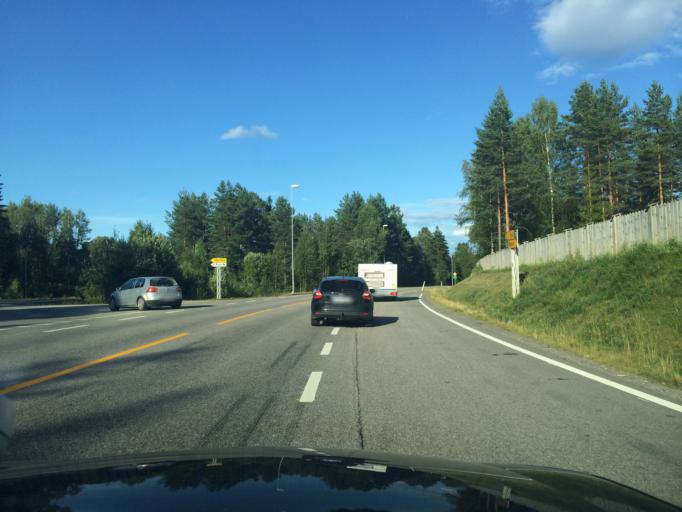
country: NO
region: Hedmark
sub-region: Elverum
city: Elverum
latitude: 60.9055
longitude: 11.6049
